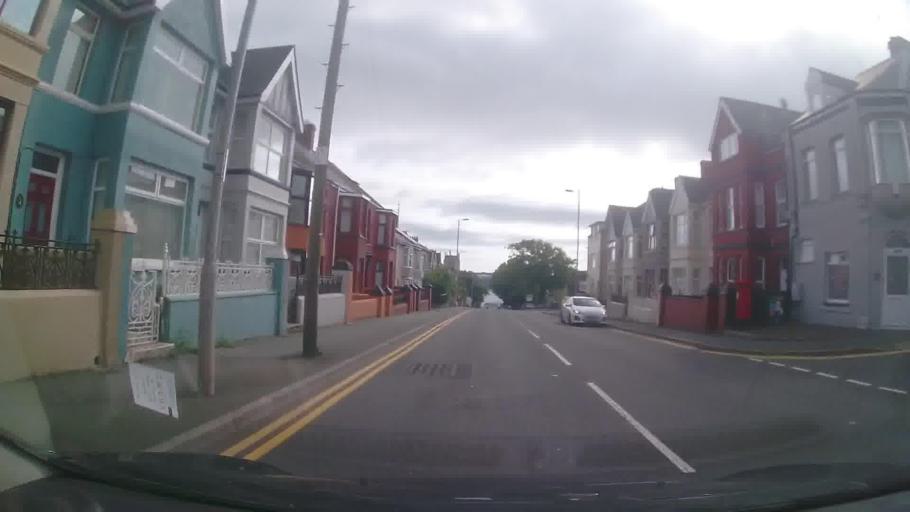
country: GB
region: Wales
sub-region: Pembrokeshire
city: Milford Haven
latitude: 51.7134
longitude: -5.0285
